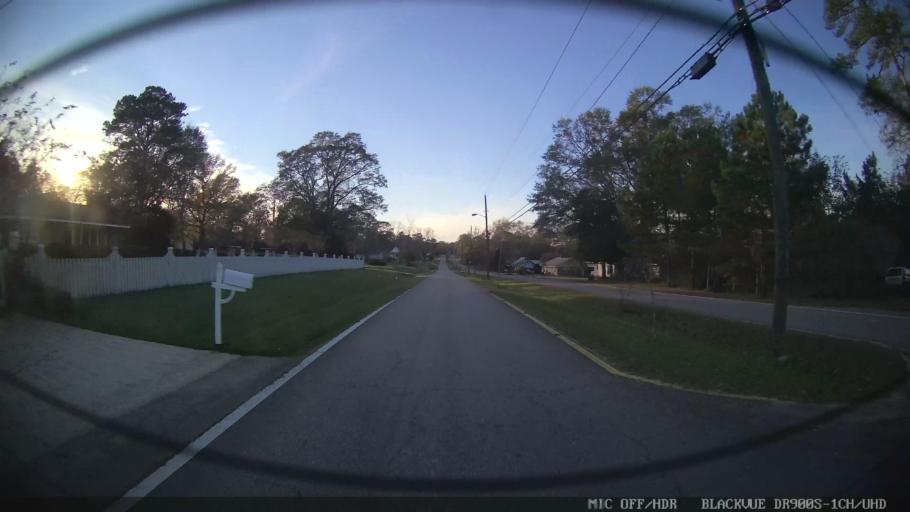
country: US
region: Mississippi
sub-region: Lamar County
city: Lumberton
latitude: 31.0041
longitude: -89.4596
